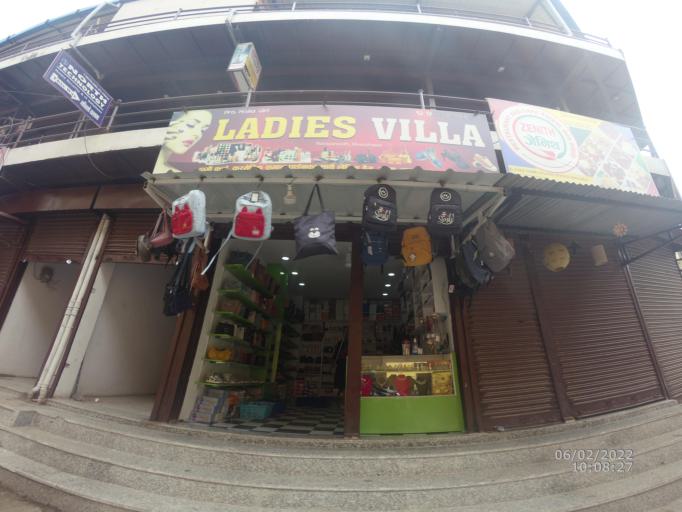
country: NP
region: Western Region
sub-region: Lumbini Zone
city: Bhairahawa
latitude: 27.5083
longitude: 83.4517
